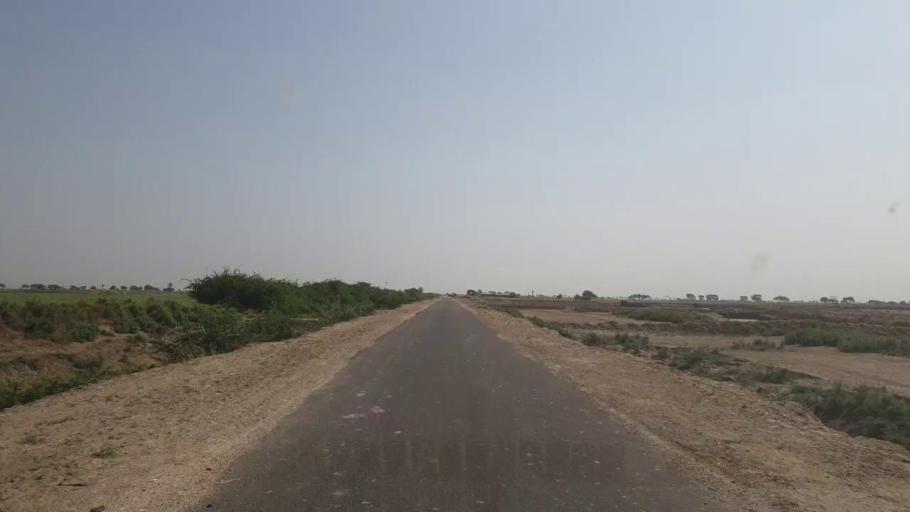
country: PK
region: Sindh
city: Jati
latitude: 24.4636
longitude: 68.5108
